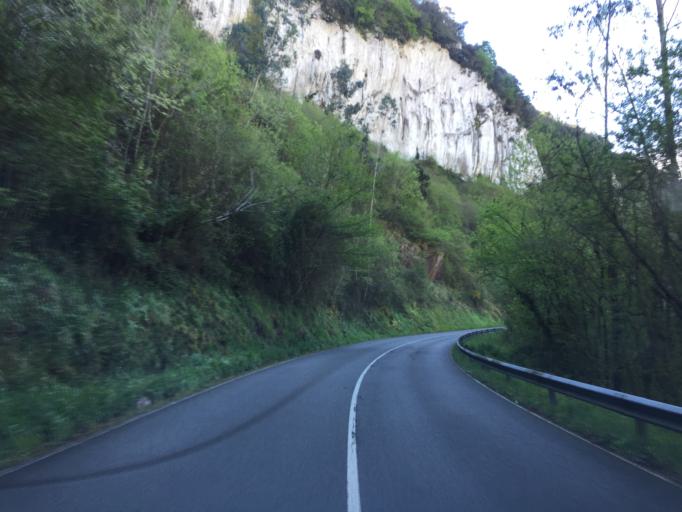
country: ES
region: Asturias
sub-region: Province of Asturias
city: Proaza
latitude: 43.3048
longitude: -5.9836
